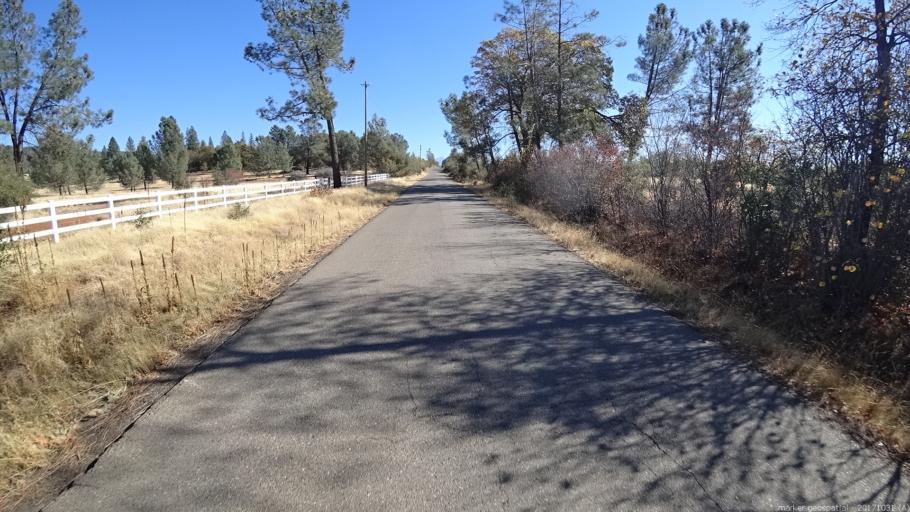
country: US
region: California
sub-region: Shasta County
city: Shingletown
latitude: 40.4463
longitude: -121.8581
